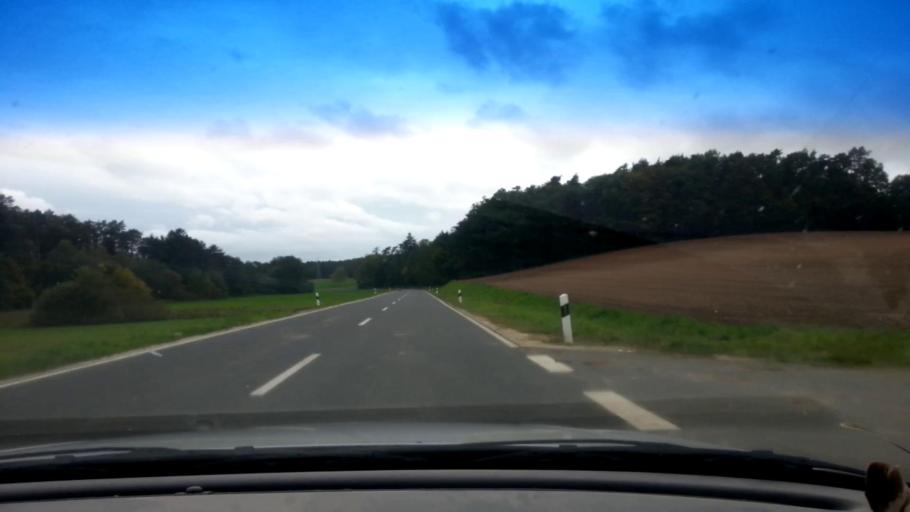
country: DE
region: Bavaria
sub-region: Upper Franconia
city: Gerach
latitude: 50.0404
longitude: 10.7846
